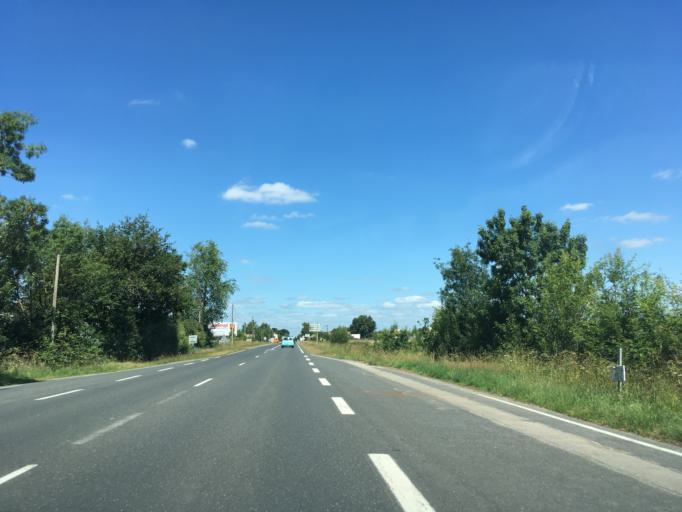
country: FR
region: Pays de la Loire
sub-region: Departement de la Loire-Atlantique
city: Les Sorinieres
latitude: 47.1383
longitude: -1.5183
